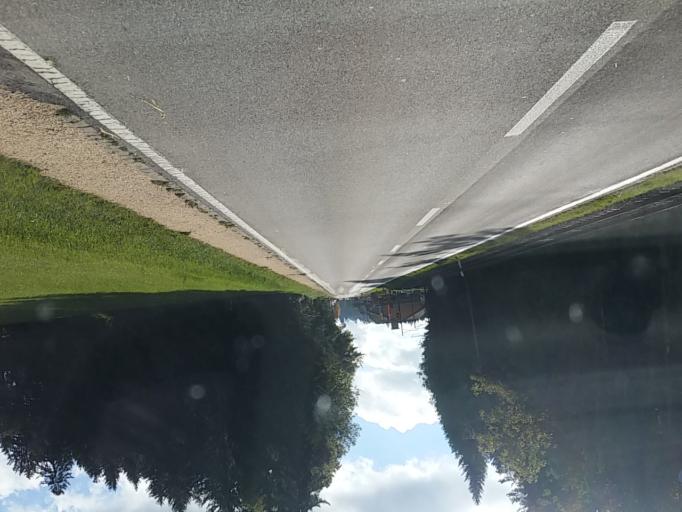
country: CH
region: Bern
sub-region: Emmental District
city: Sumiswald
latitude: 47.0653
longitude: 7.7490
